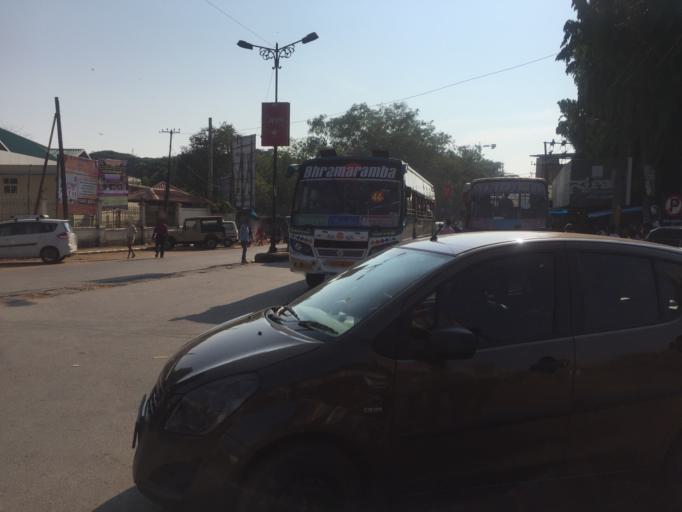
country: IN
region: Karnataka
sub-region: Dakshina Kannada
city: Mangalore
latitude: 12.8648
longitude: 74.8389
